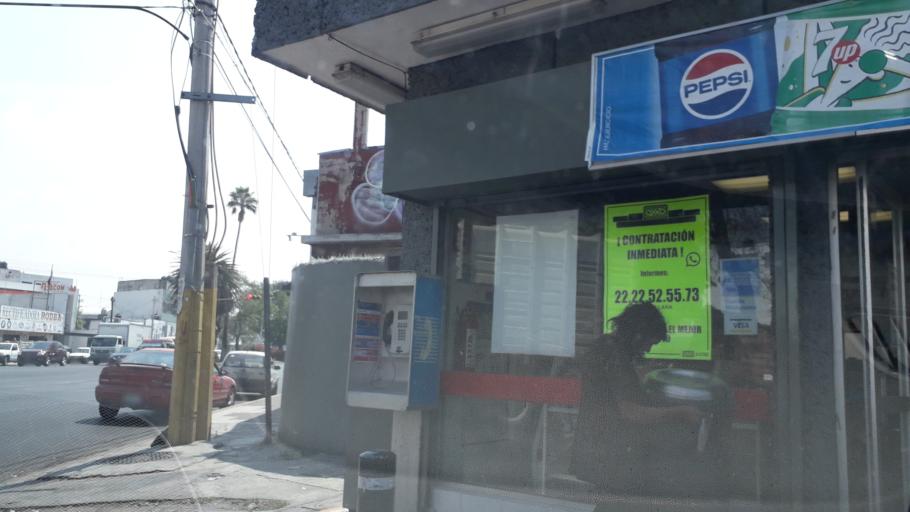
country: MX
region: Puebla
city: Puebla
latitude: 19.0551
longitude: -98.2177
